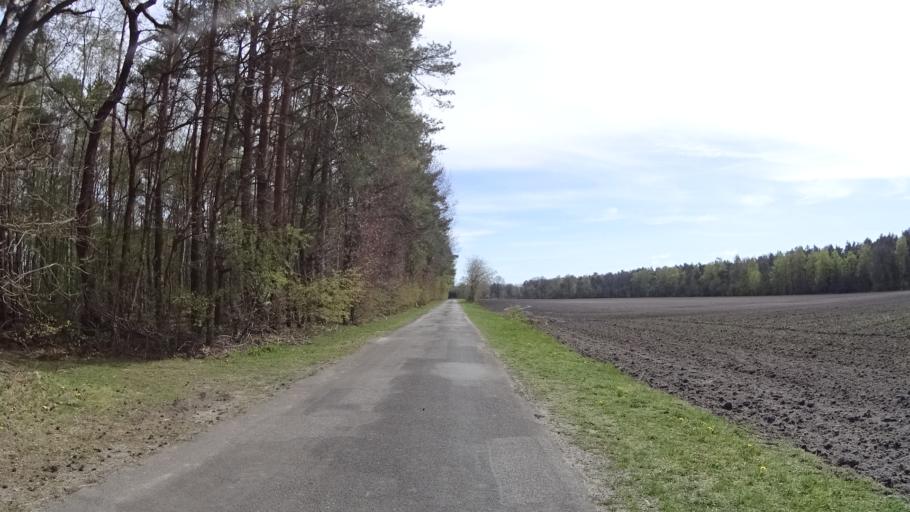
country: DE
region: Lower Saxony
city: Lunne
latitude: 52.3791
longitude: 7.3992
